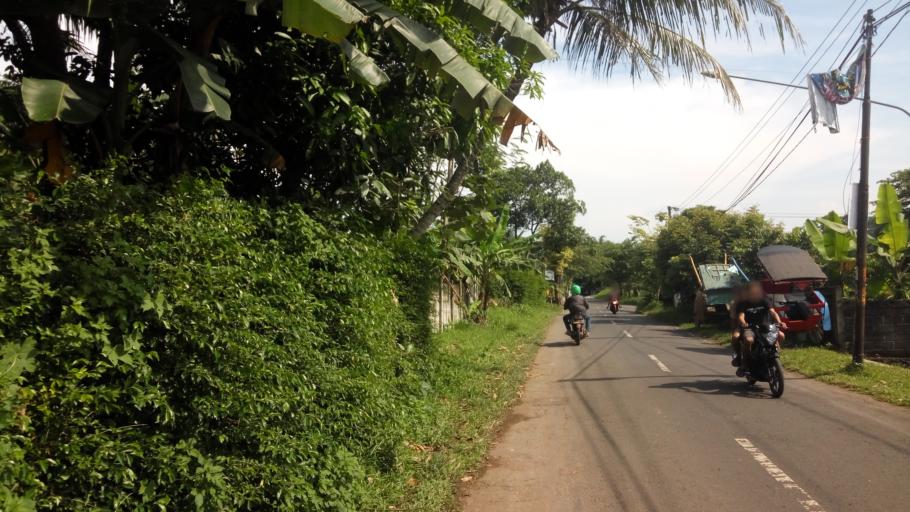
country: ID
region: Central Java
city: Ungaran
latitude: -7.1308
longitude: 110.4227
